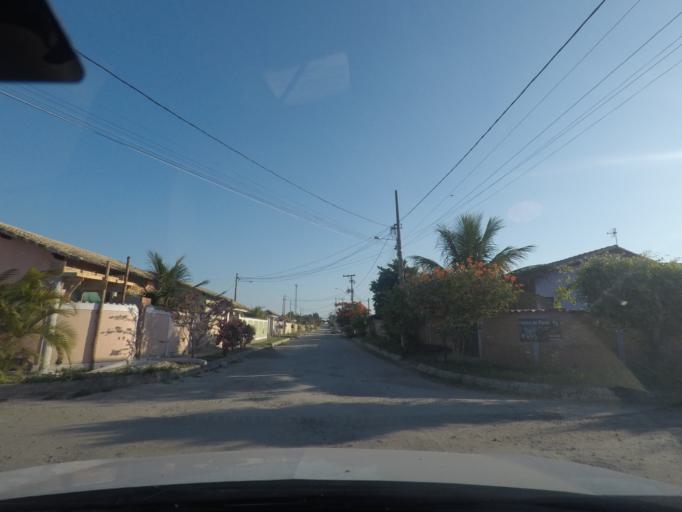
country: BR
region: Rio de Janeiro
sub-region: Marica
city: Marica
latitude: -22.9645
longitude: -42.9343
